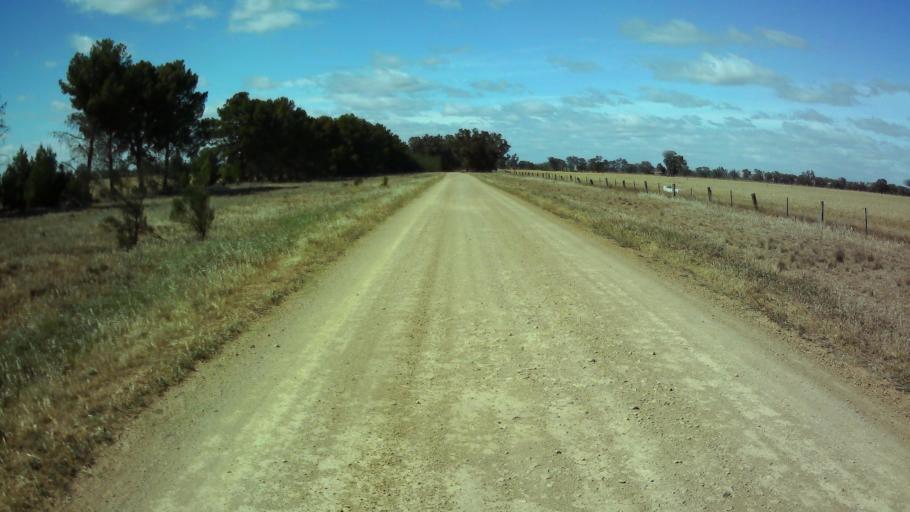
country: AU
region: New South Wales
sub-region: Weddin
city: Grenfell
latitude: -34.0332
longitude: 148.3170
